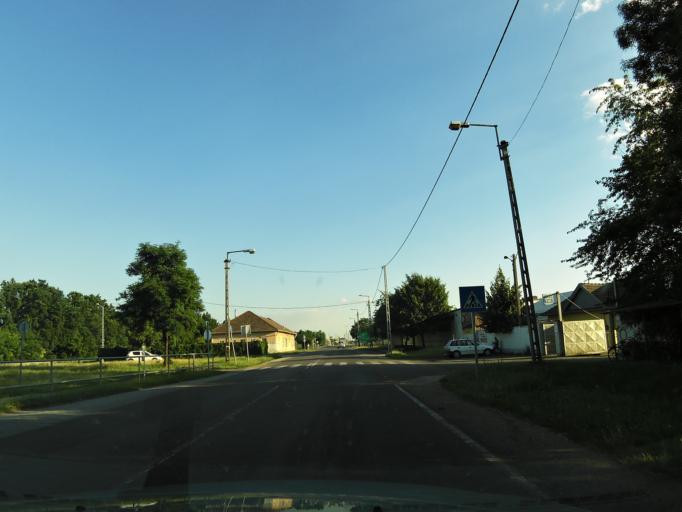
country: HU
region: Jasz-Nagykun-Szolnok
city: Rakocziujfalu
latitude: 47.0206
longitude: 20.2913
